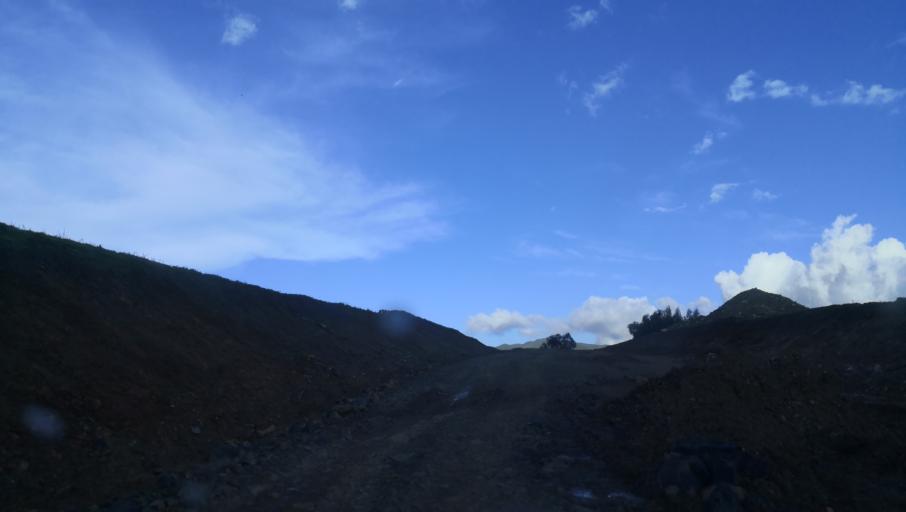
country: ET
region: Southern Nations, Nationalities, and People's Region
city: Butajira
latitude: 8.3991
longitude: 38.3203
